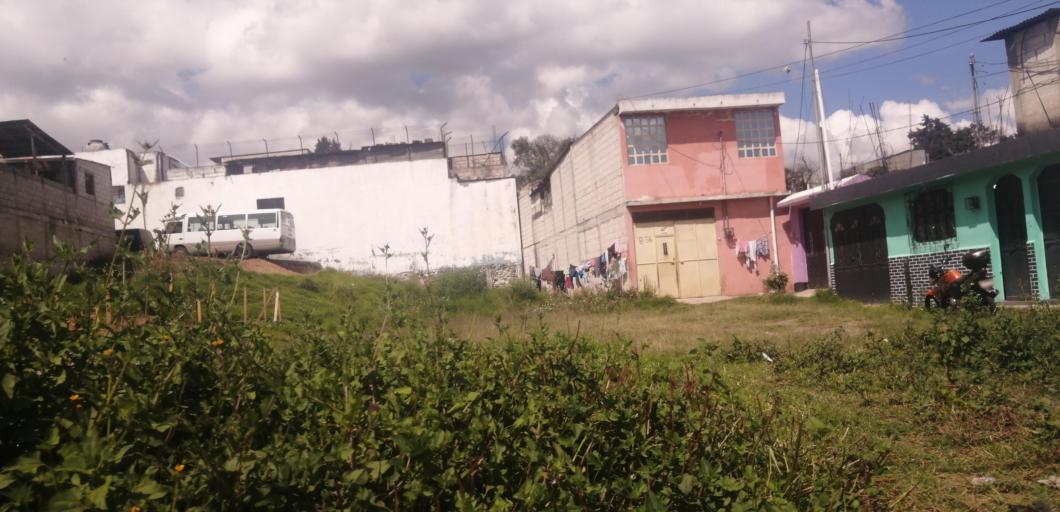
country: GT
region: Quetzaltenango
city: Quetzaltenango
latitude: 14.8340
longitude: -91.5302
